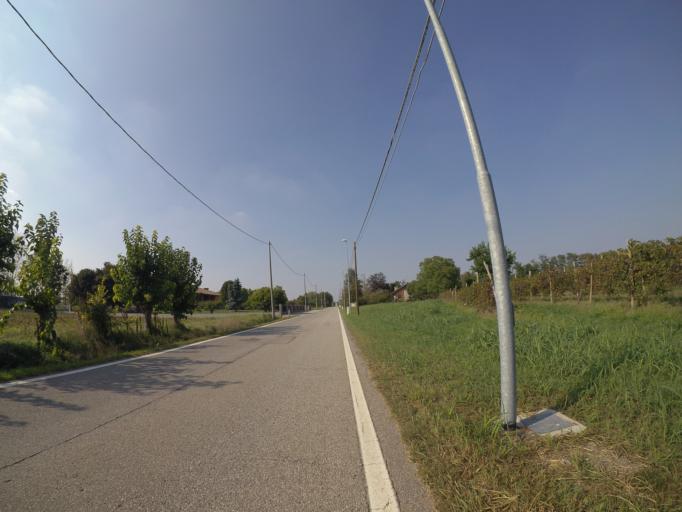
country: IT
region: Friuli Venezia Giulia
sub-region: Provincia di Udine
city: Basiliano
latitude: 45.9875
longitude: 13.0323
